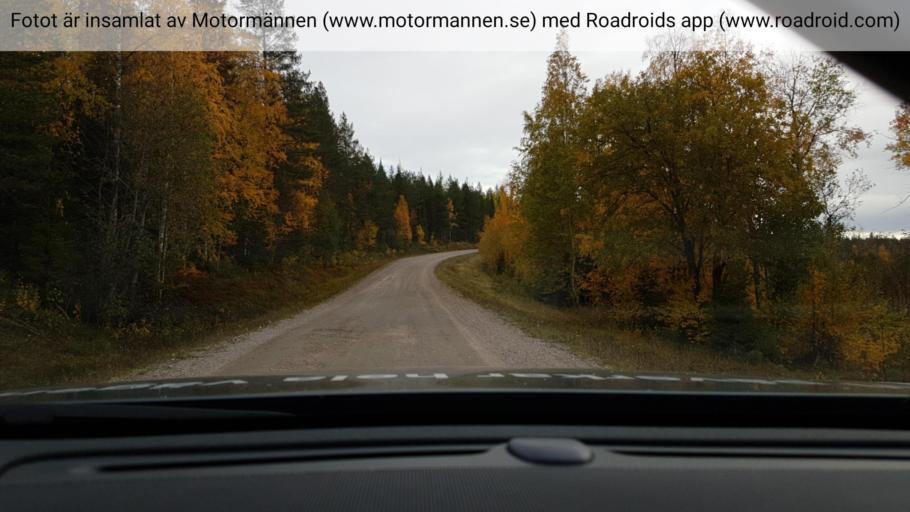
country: SE
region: Norrbotten
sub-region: Overkalix Kommun
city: OEverkalix
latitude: 66.2637
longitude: 23.0225
